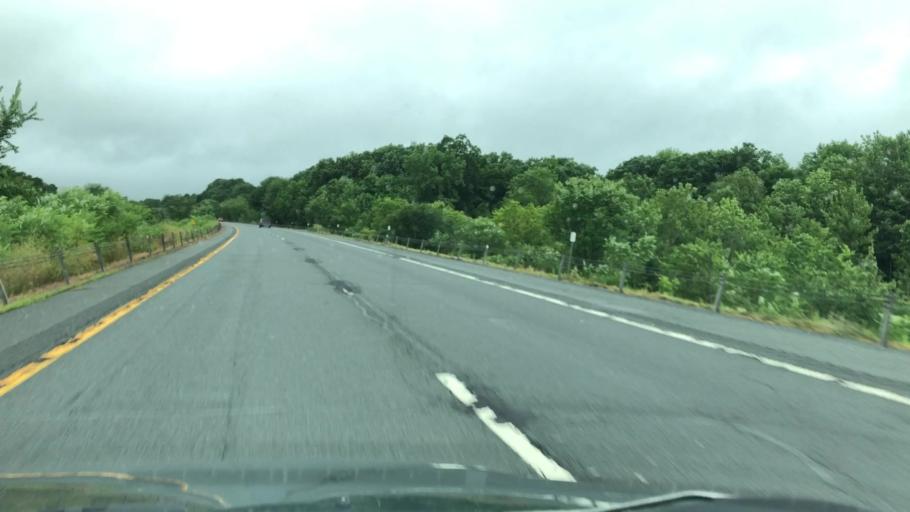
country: US
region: New York
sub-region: Orange County
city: Middletown
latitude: 41.4075
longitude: -74.4908
